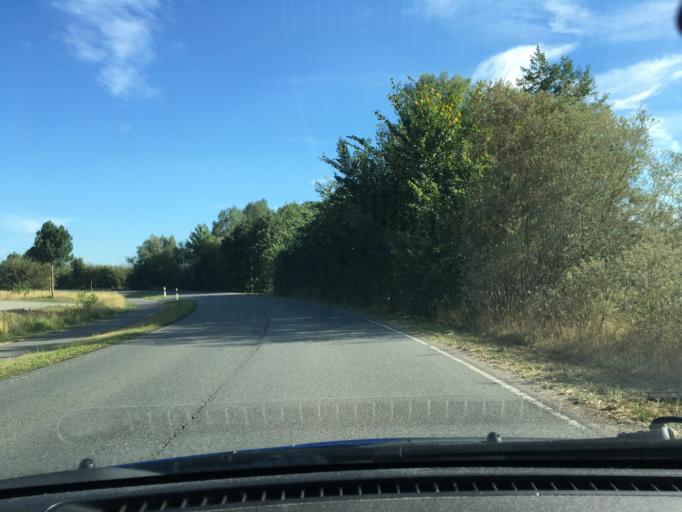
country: DE
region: Lower Saxony
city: Bleckede
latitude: 53.2970
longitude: 10.7149
